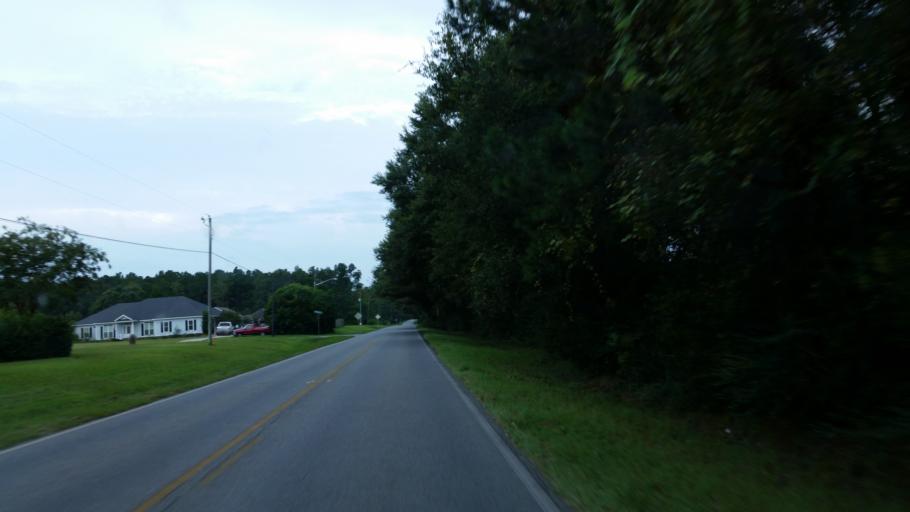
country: US
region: Georgia
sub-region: Lowndes County
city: Valdosta
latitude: 30.7579
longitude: -83.2591
